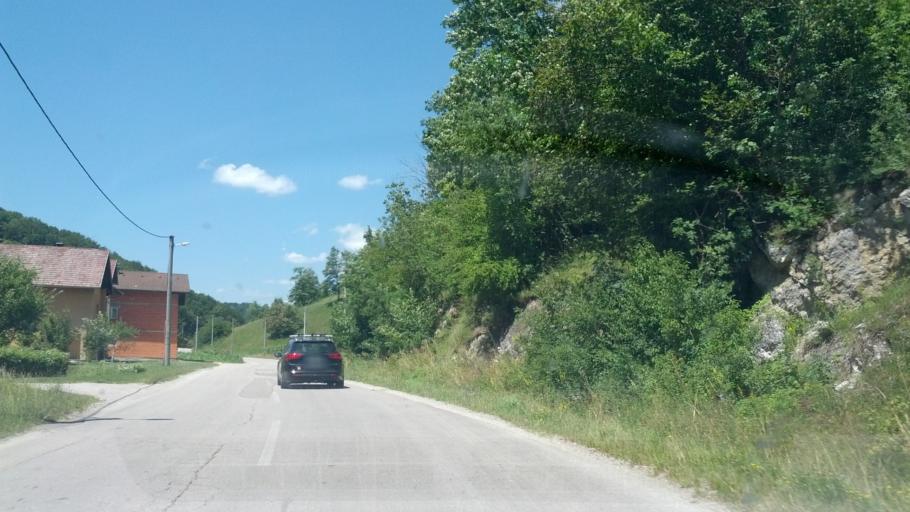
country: BA
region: Federation of Bosnia and Herzegovina
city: Jezerski
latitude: 45.0217
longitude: 16.0871
